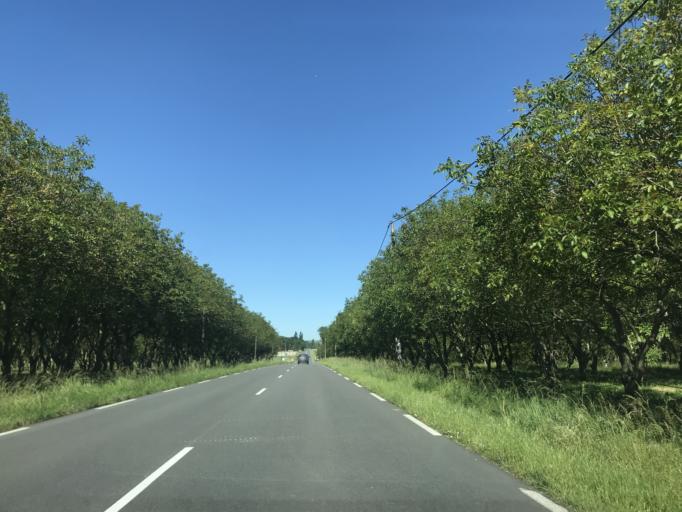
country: FR
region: Poitou-Charentes
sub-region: Departement de la Charente
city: Barbezieux-Saint-Hilaire
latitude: 45.4960
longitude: -0.2267
